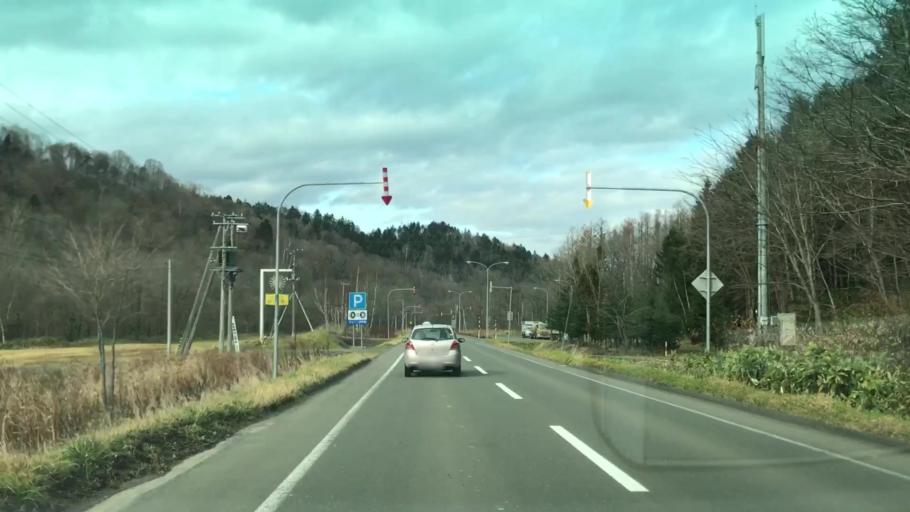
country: JP
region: Hokkaido
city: Shimo-furano
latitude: 42.9273
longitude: 142.4446
